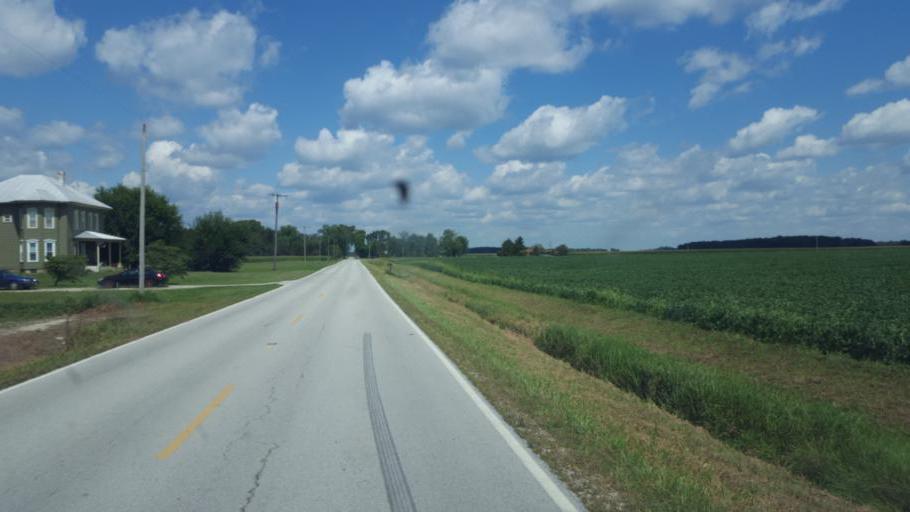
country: US
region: Ohio
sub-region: Sandusky County
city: Gibsonburg
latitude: 41.2874
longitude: -83.3110
